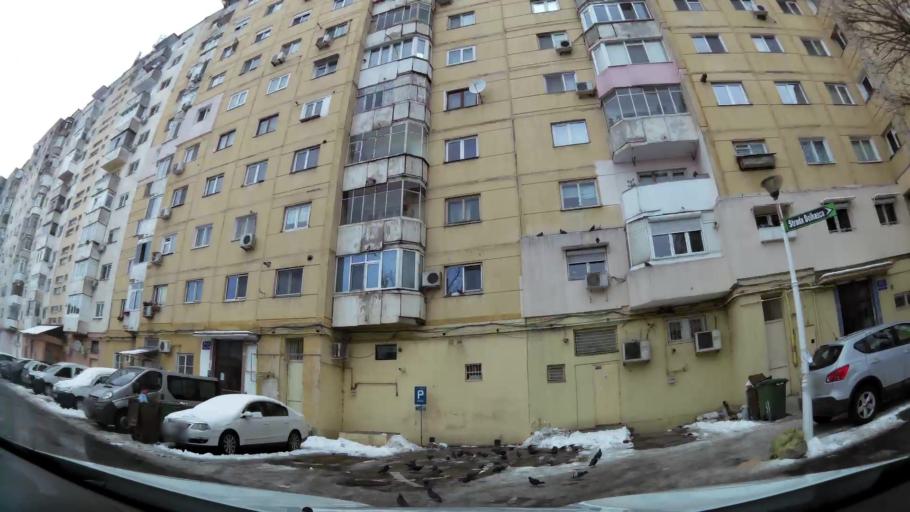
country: RO
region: Bucuresti
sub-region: Municipiul Bucuresti
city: Bucuresti
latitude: 44.3949
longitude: 26.1169
